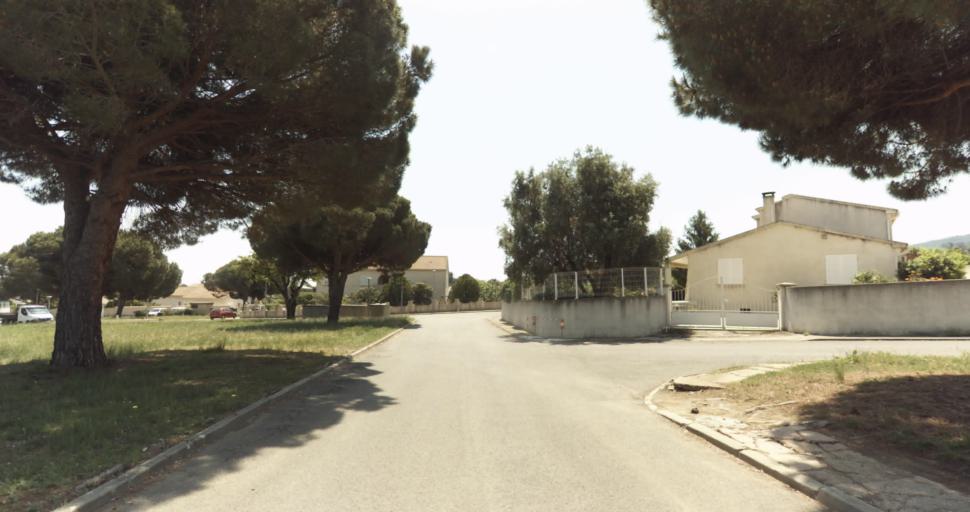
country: FR
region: Corsica
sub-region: Departement de la Haute-Corse
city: Biguglia
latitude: 42.5944
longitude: 9.4311
